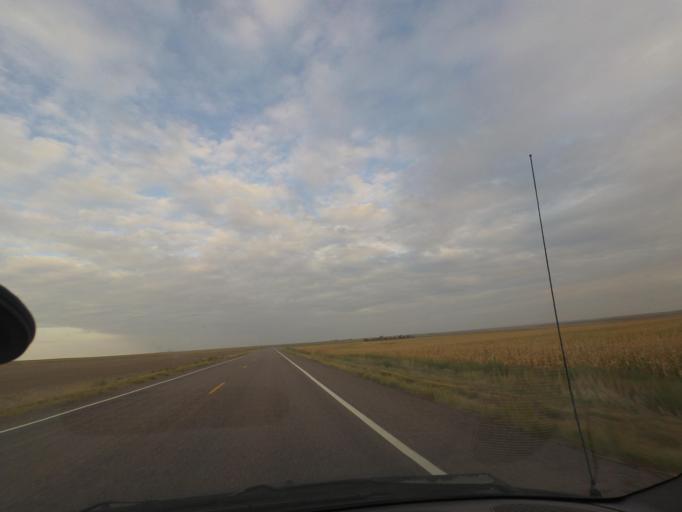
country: US
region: Kansas
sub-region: Cheyenne County
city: Saint Francis
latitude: 39.7464
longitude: -102.0998
